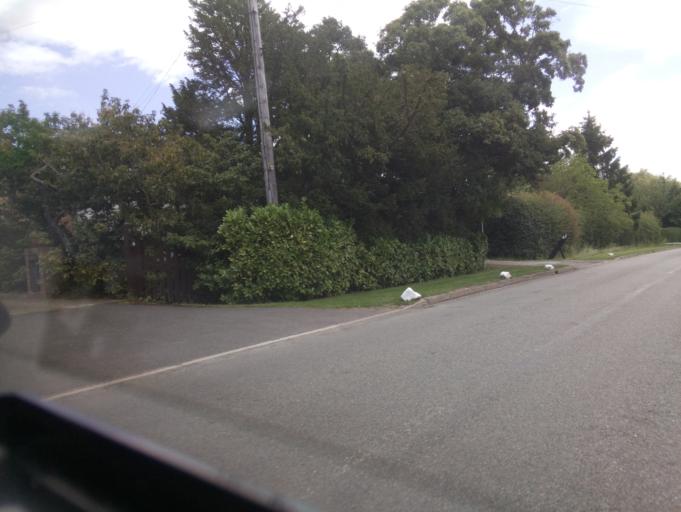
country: GB
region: England
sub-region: Nottinghamshire
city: Cotgrave
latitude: 52.8697
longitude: -1.0687
